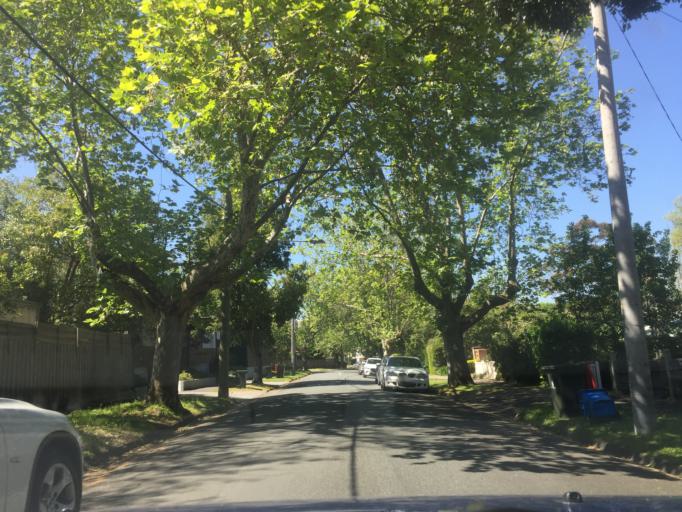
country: AU
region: Victoria
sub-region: Boroondara
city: Canterbury
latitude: -37.8251
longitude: 145.0762
